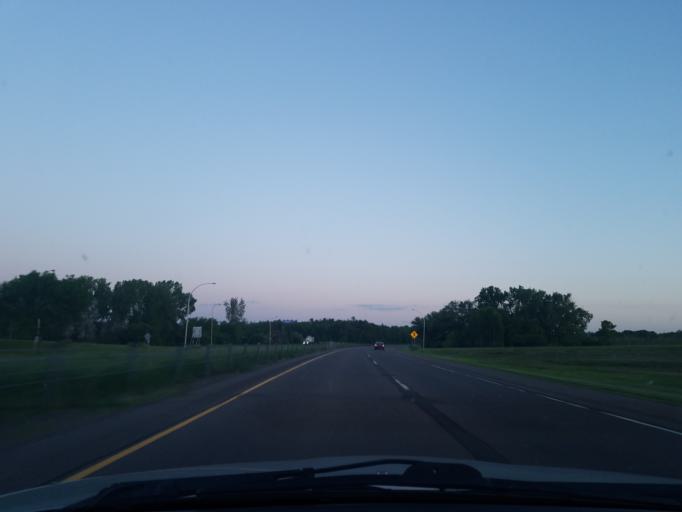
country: US
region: Minnesota
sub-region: Pine County
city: Pine City
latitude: 45.8212
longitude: -92.9836
